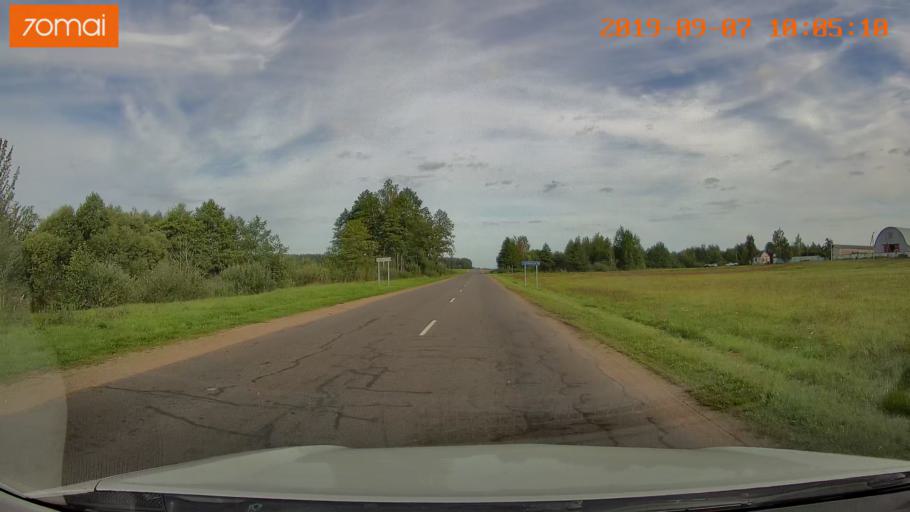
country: BY
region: Grodnenskaya
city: Voranava
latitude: 54.0439
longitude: 25.4087
